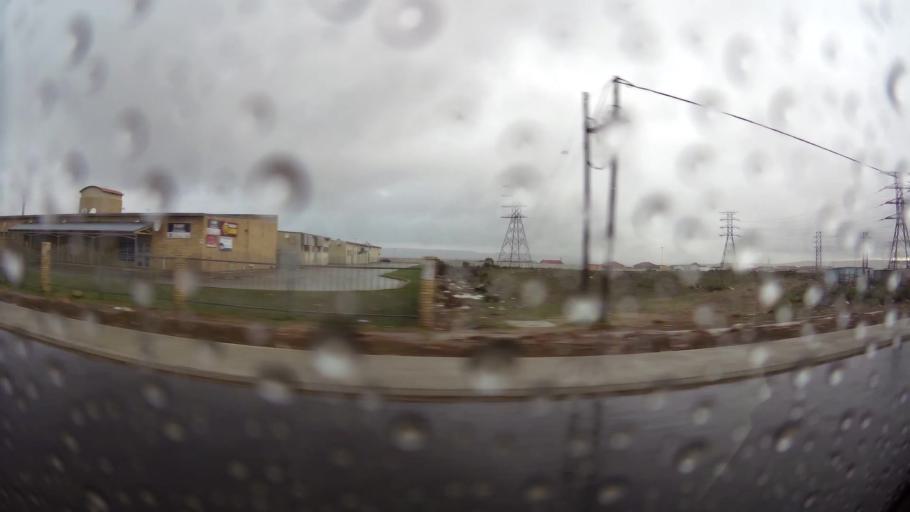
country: ZA
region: Eastern Cape
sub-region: Nelson Mandela Bay Metropolitan Municipality
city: Port Elizabeth
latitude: -33.8383
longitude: 25.5215
